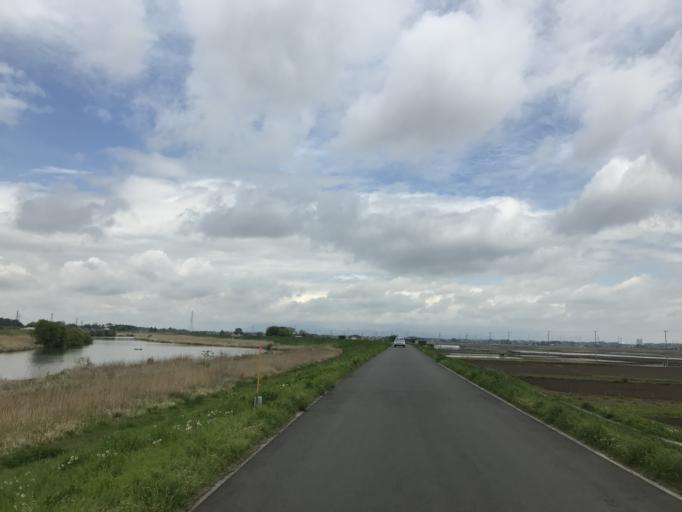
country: JP
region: Ibaraki
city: Mitsukaido
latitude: 35.9938
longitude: 139.9912
